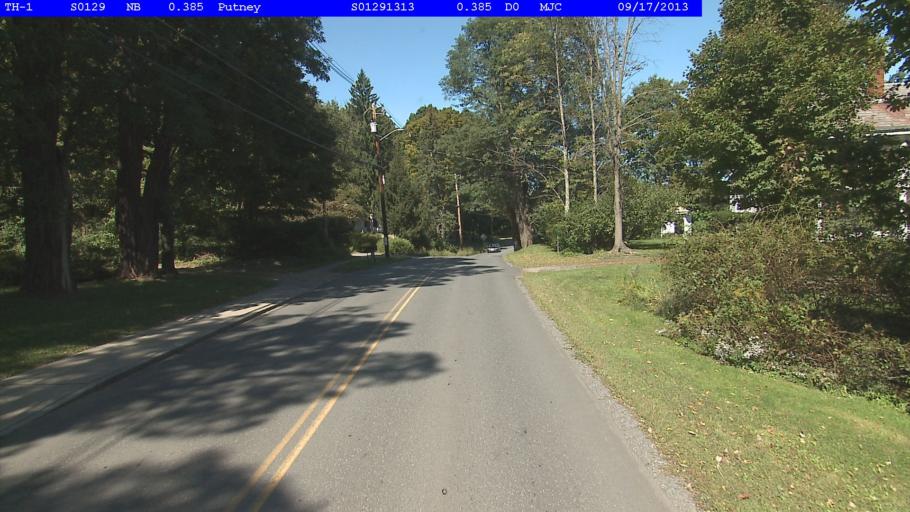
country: US
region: New Hampshire
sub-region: Cheshire County
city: Westmoreland
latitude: 42.9785
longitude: -72.5273
